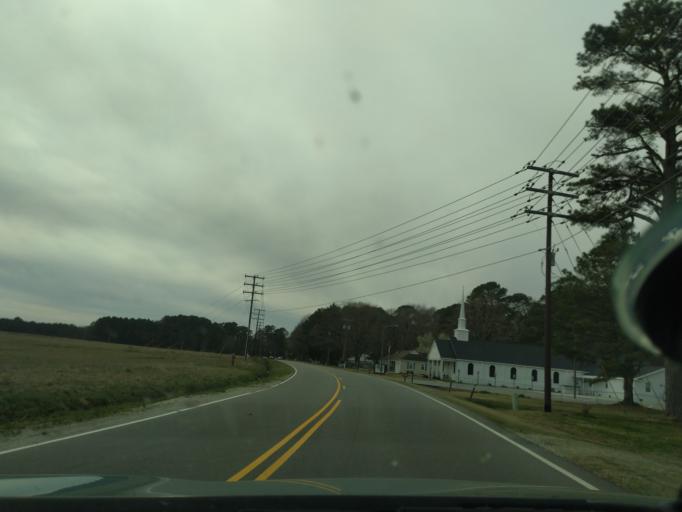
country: US
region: North Carolina
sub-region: Edgecombe County
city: Tarboro
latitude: 35.8951
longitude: -77.5866
